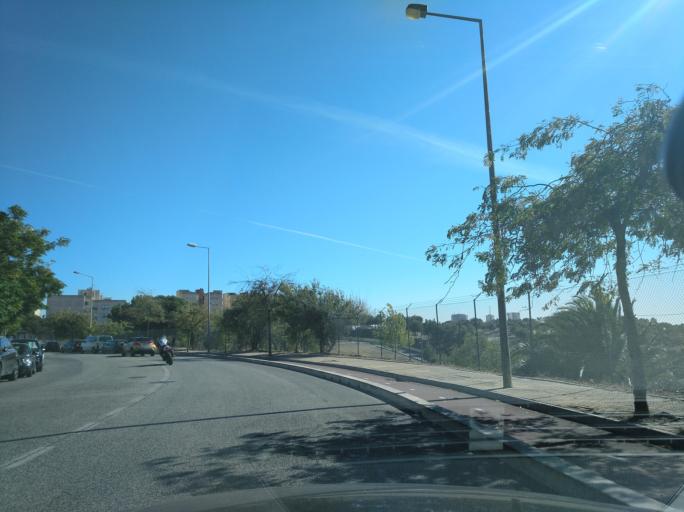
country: PT
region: Lisbon
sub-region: Loures
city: Moscavide
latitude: 38.7560
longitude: -9.1271
